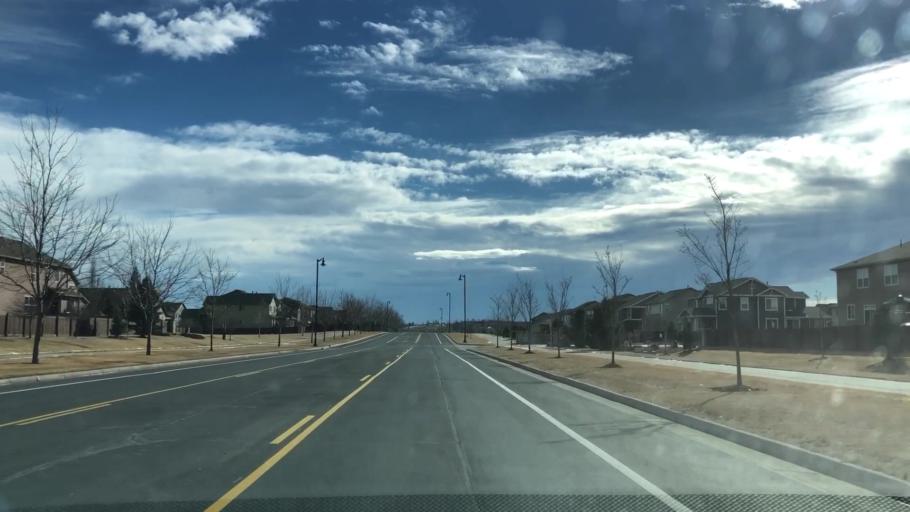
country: US
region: Colorado
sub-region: Weld County
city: Windsor
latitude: 40.5062
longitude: -104.9630
